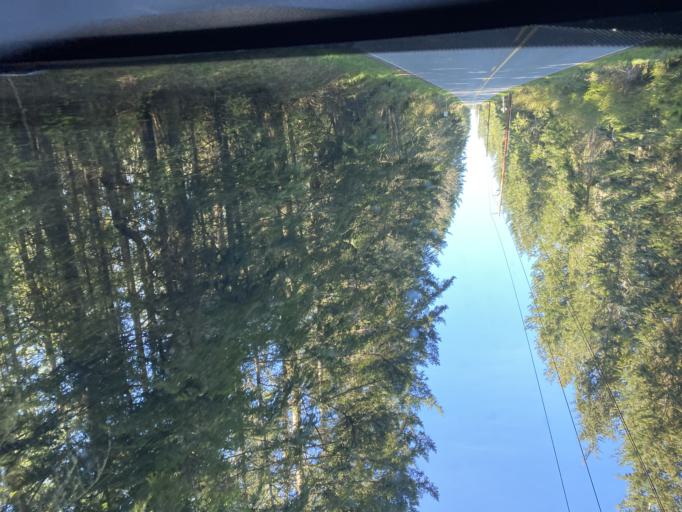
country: US
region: Washington
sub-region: Island County
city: Freeland
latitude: 48.0808
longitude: -122.5830
